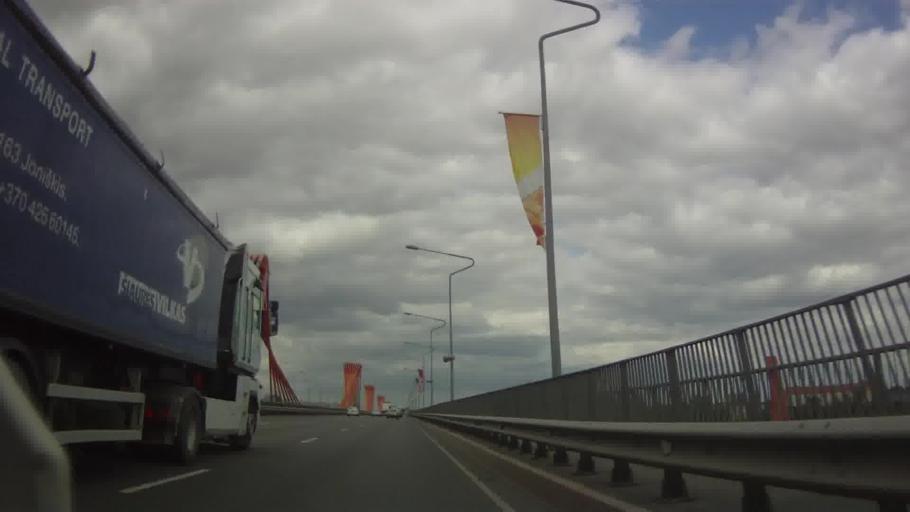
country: LV
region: Kekava
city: Balozi
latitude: 56.9142
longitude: 24.1551
